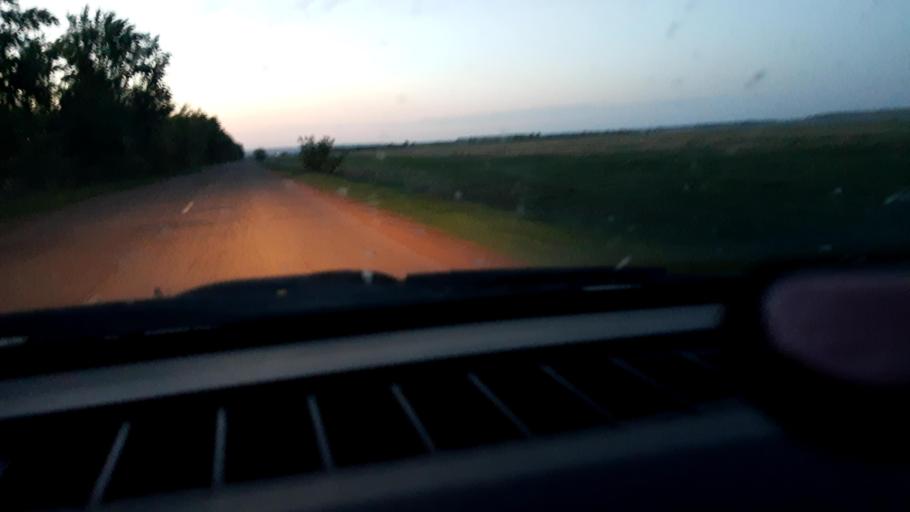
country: RU
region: Bashkortostan
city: Asanovo
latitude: 54.8358
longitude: 55.6012
